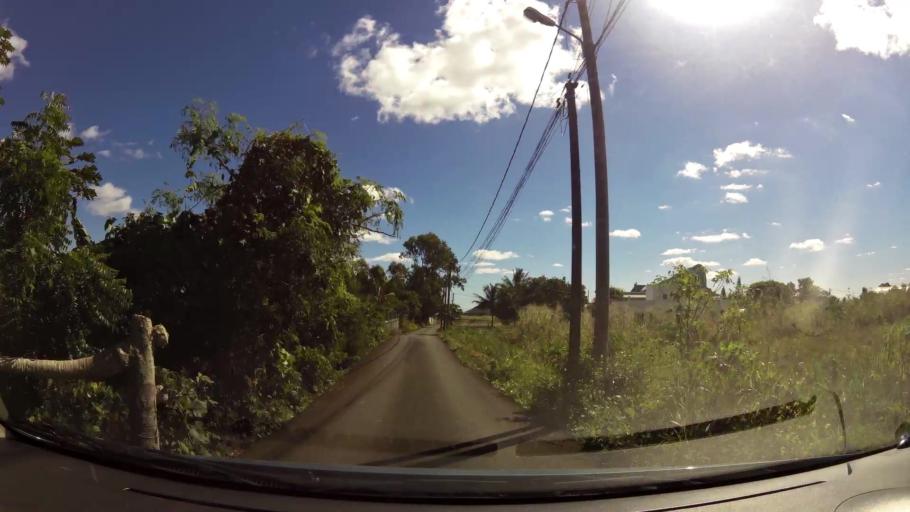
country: MU
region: Plaines Wilhems
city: Vacoas
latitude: -20.2932
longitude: 57.4727
